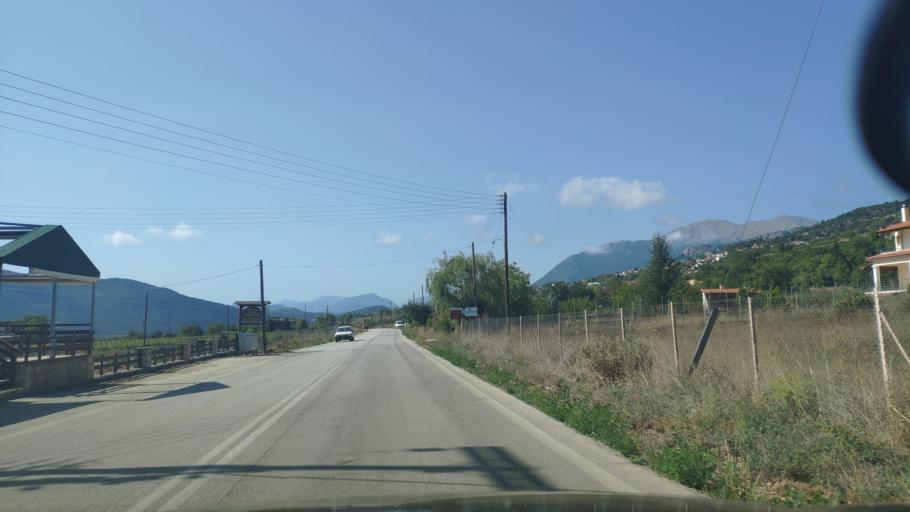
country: GR
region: Peloponnese
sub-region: Nomos Korinthias
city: Xylokastro
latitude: 37.9585
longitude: 22.5788
